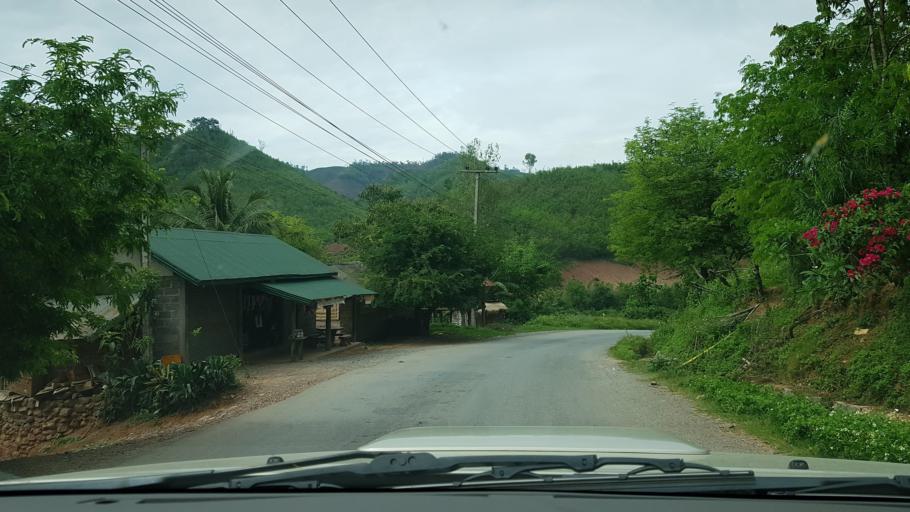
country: LA
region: Loungnamtha
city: Muang Nale
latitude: 20.3672
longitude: 101.7126
